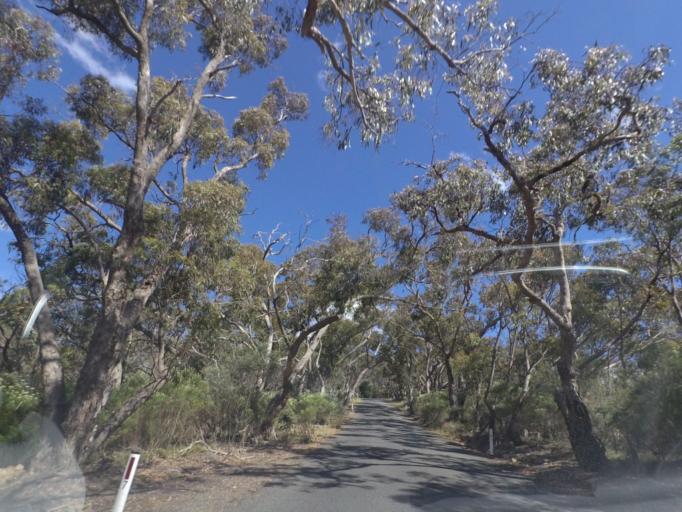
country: AU
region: Victoria
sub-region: Hume
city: Sunbury
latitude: -37.4220
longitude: 144.6354
